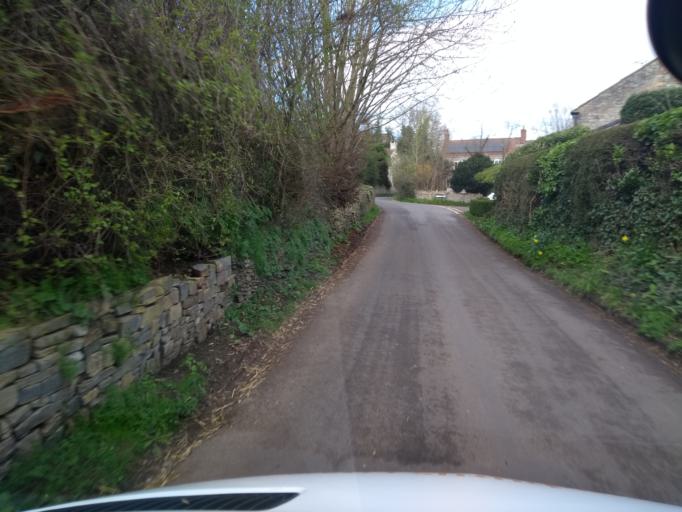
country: GB
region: England
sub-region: Somerset
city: Westonzoyland
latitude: 51.1273
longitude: -2.8591
